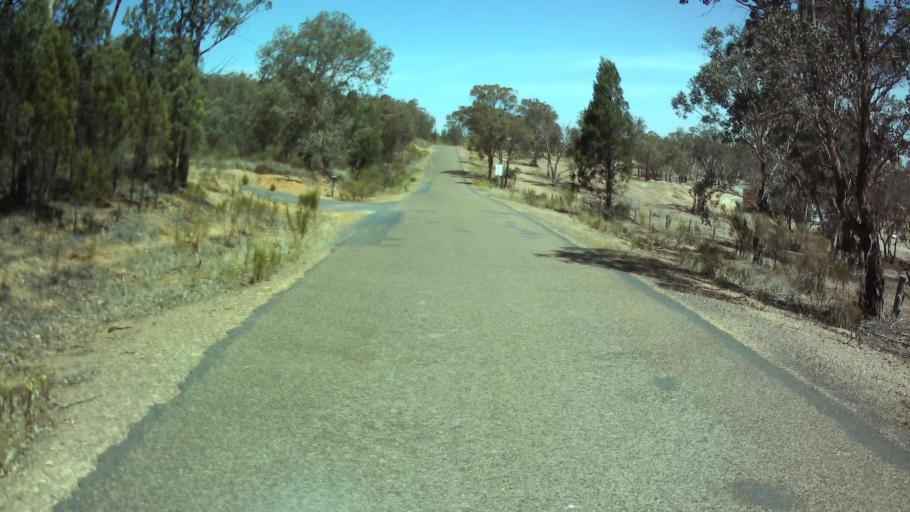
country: AU
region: New South Wales
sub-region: Weddin
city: Grenfell
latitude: -33.9045
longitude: 148.1784
